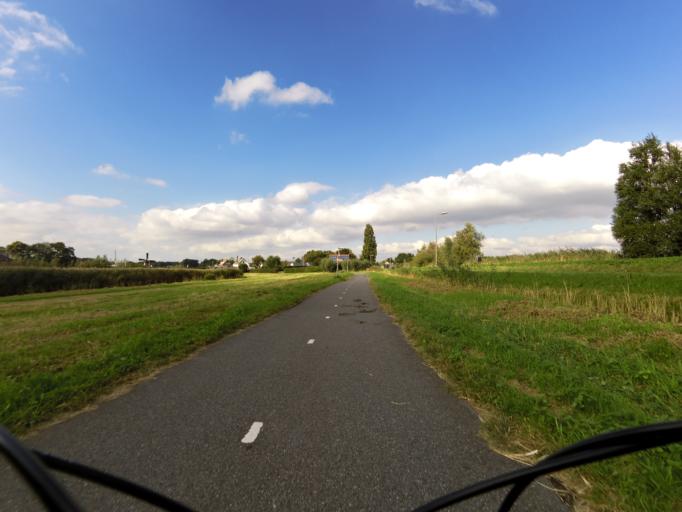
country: NL
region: South Holland
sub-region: Gemeente Voorschoten
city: Voorschoten
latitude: 52.1039
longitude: 4.4380
